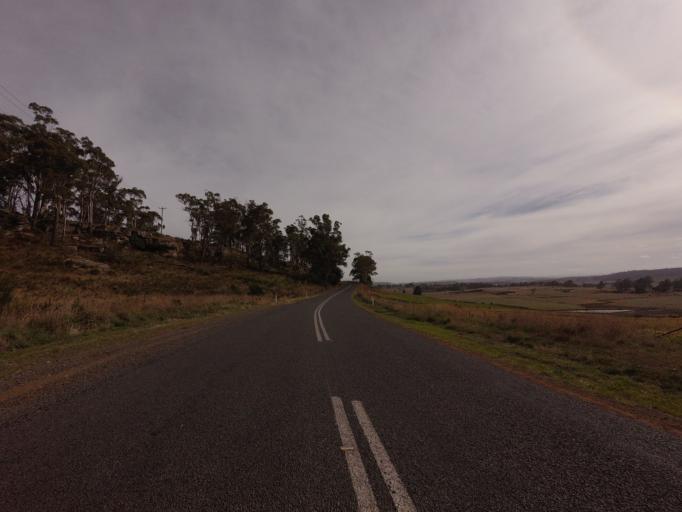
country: AU
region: Tasmania
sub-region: Brighton
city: Bridgewater
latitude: -42.3759
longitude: 147.4229
